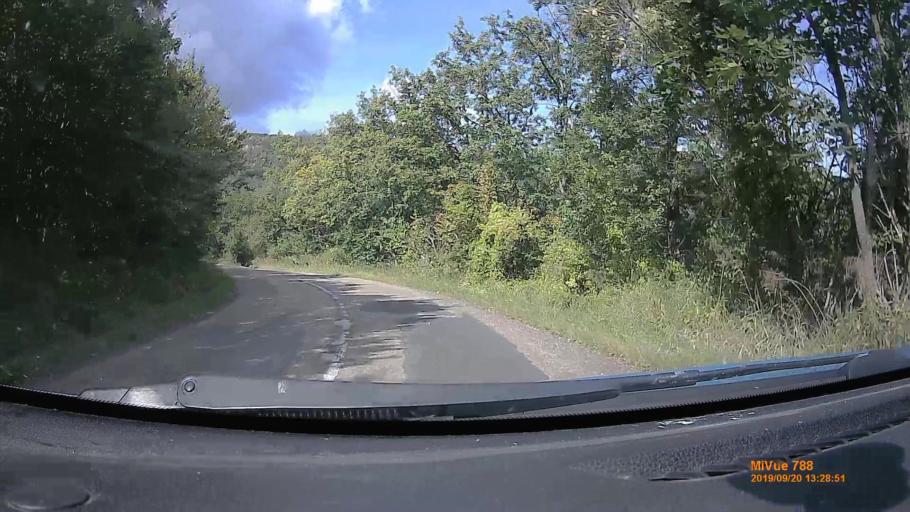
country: HU
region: Heves
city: Szilvasvarad
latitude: 48.0497
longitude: 20.4843
